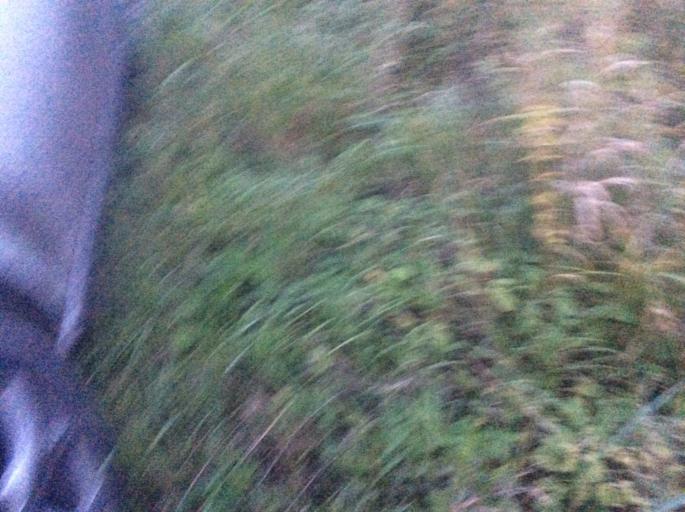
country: RU
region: Vologda
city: Ferapontovo
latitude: 59.9633
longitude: 38.5905
